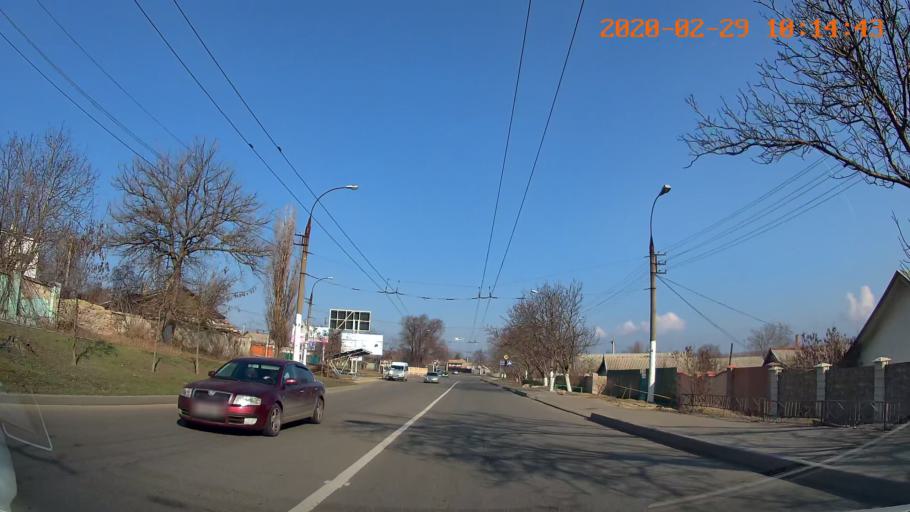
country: MD
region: Telenesti
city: Tiraspolul Nou
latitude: 46.8494
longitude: 29.6433
